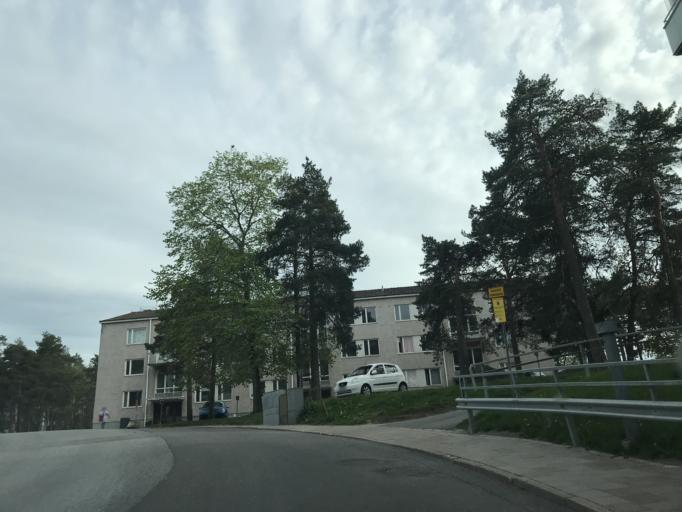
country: FI
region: Varsinais-Suomi
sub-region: Turku
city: Turku
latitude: 60.4351
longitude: 22.3022
